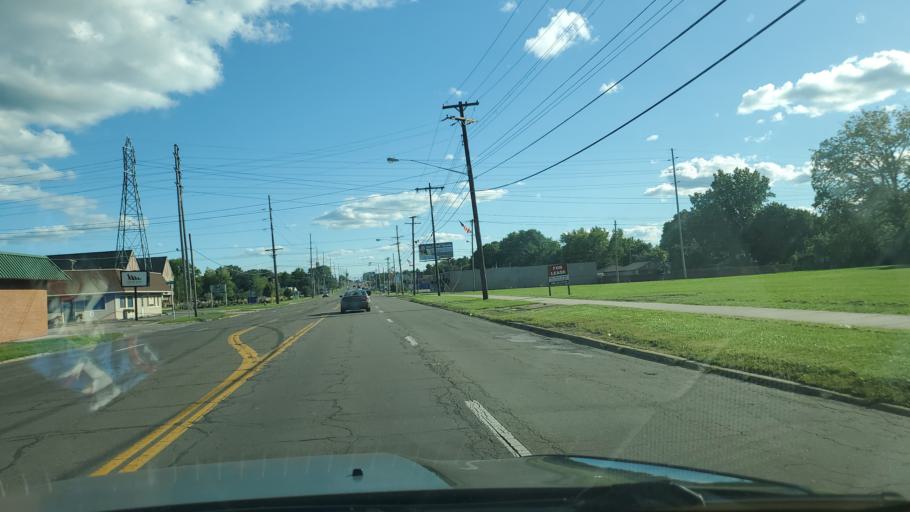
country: US
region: Ohio
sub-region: Mahoning County
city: Boardman
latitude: 41.0346
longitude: -80.6628
